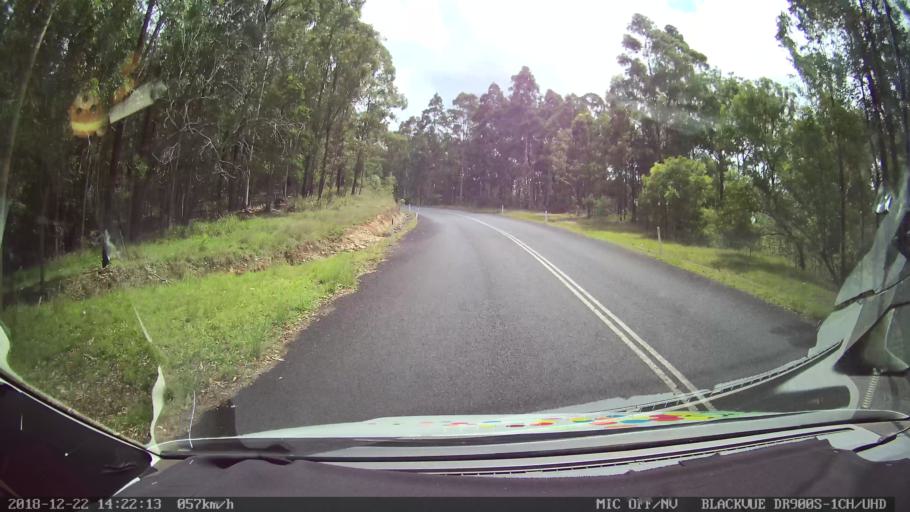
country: AU
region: New South Wales
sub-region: Clarence Valley
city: Coutts Crossing
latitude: -30.0243
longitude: 152.6545
